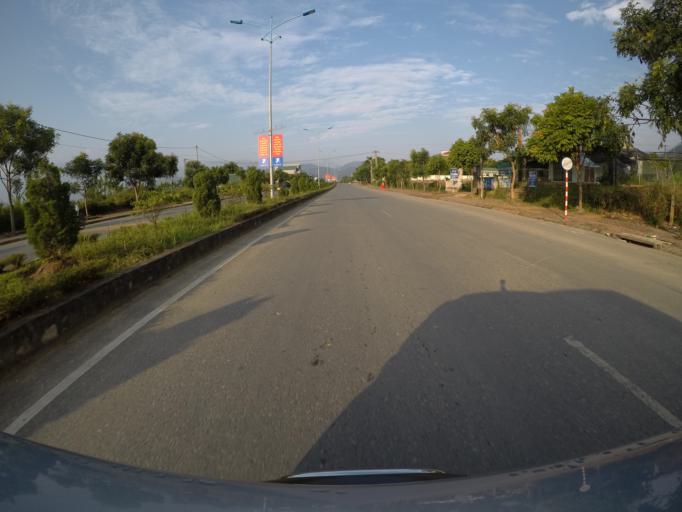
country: VN
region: Lai Chau
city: Tam Duong
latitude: 22.3199
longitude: 103.6355
